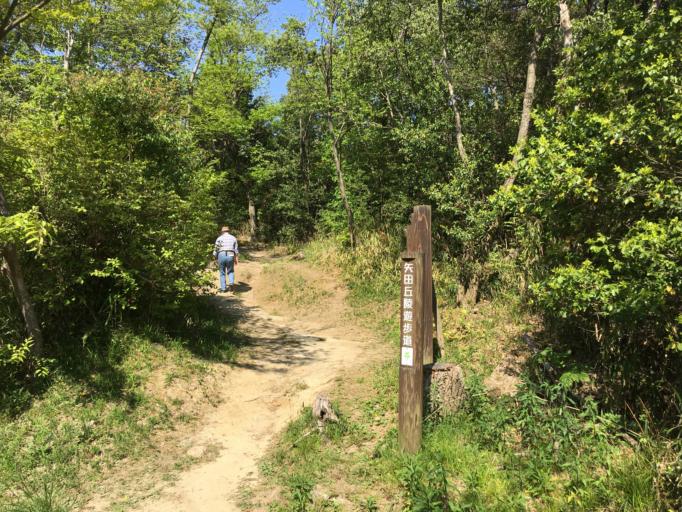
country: JP
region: Nara
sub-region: Ikoma-shi
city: Ikoma
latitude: 34.6950
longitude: 135.7173
